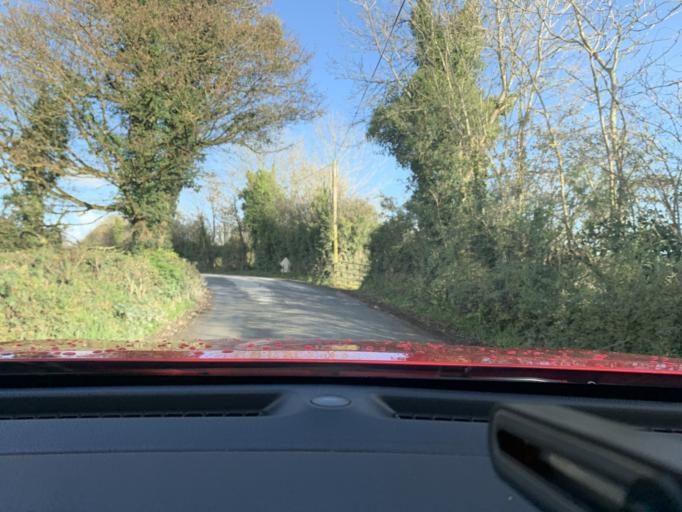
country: IE
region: Connaught
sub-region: Sligo
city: Ballymote
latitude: 54.1098
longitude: -8.4212
